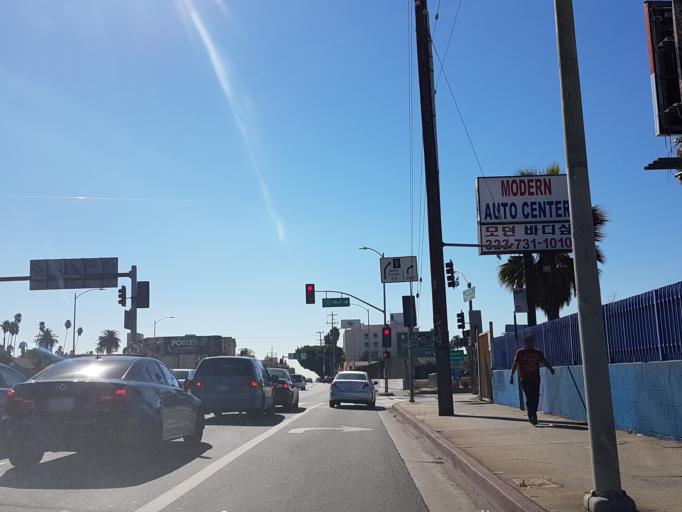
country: US
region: California
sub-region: Los Angeles County
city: View Park-Windsor Hills
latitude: 34.0381
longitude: -118.3091
